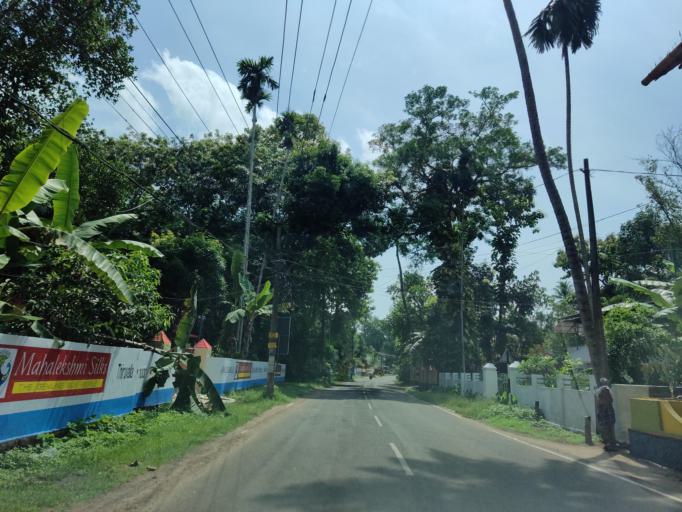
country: IN
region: Kerala
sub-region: Alappuzha
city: Chengannur
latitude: 9.3085
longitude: 76.5695
